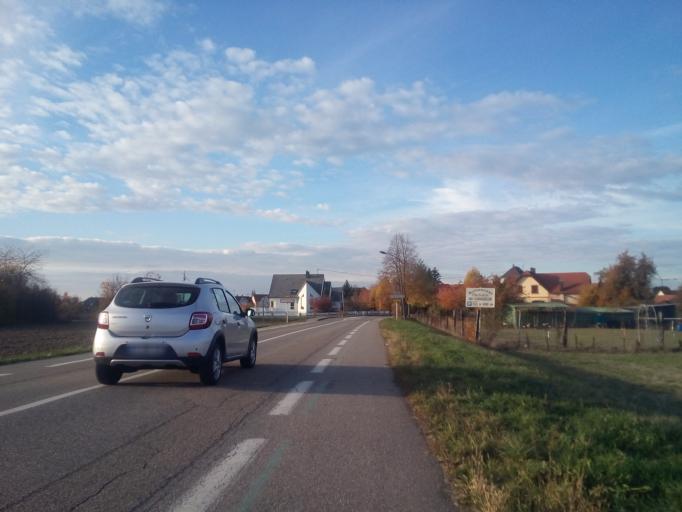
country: FR
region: Alsace
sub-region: Departement du Bas-Rhin
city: Herrlisheim
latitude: 48.7224
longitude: 7.9099
